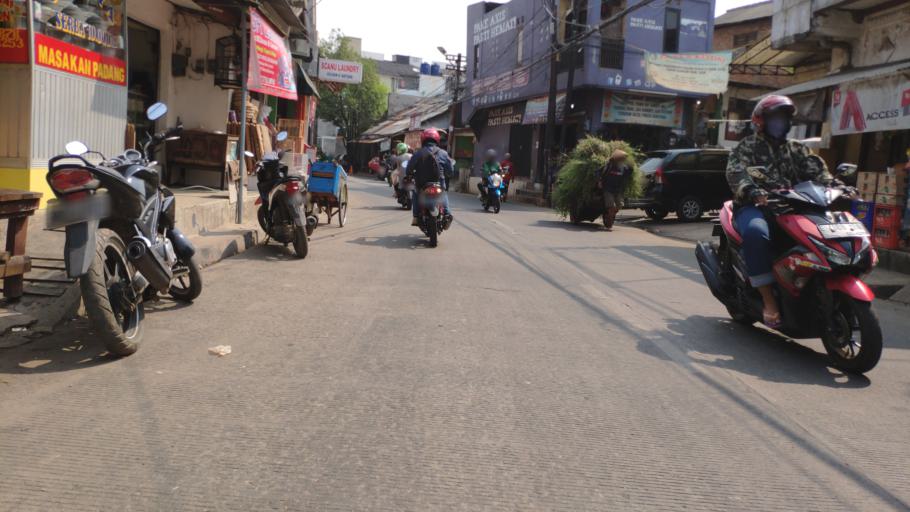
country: ID
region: Jakarta Raya
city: Jakarta
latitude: -6.2559
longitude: 106.8245
